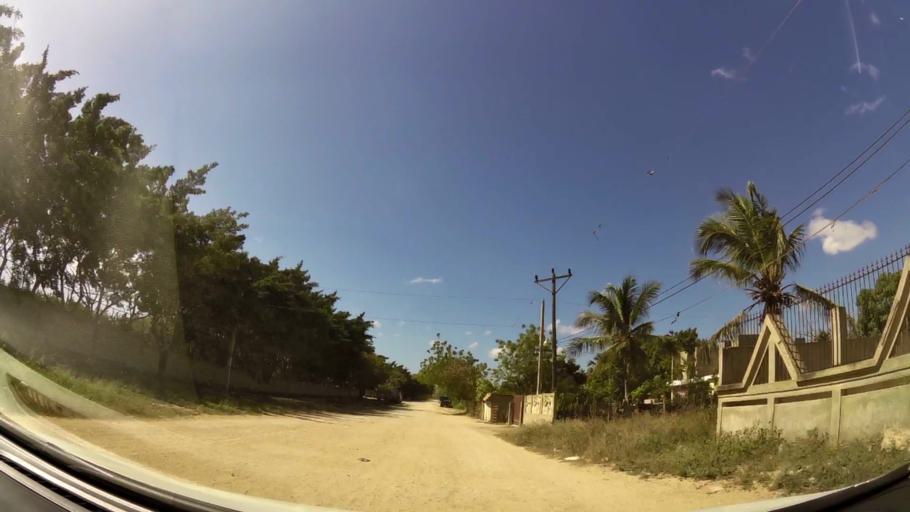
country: DO
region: Santo Domingo
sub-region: Santo Domingo
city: Boca Chica
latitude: 18.4594
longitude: -69.6247
